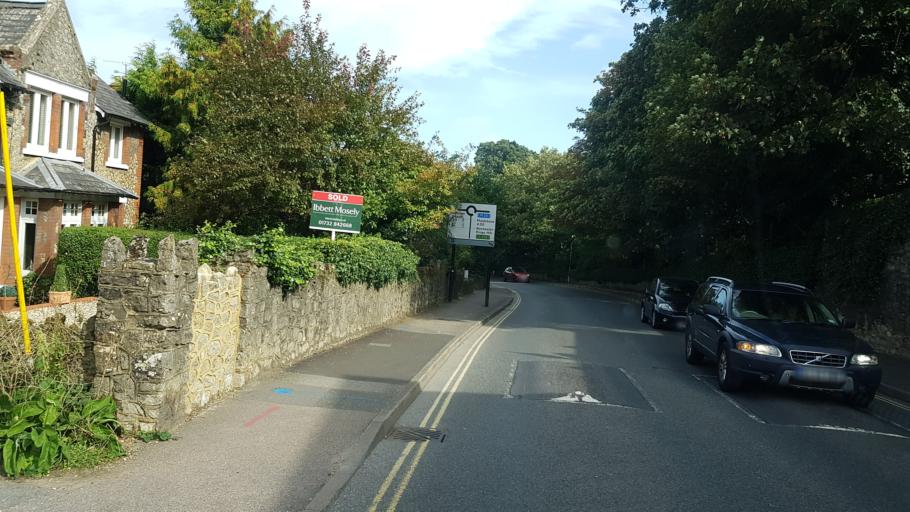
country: GB
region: England
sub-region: Kent
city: West Malling
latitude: 51.2974
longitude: 0.4107
